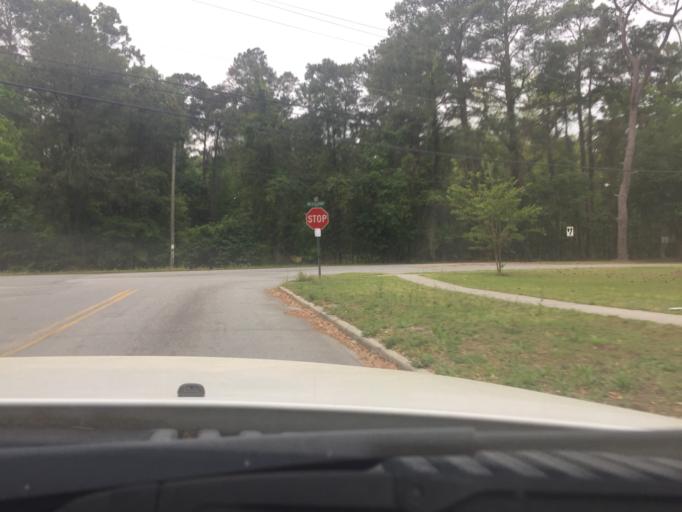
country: US
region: Georgia
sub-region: Chatham County
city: Georgetown
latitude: 31.9718
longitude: -81.2274
